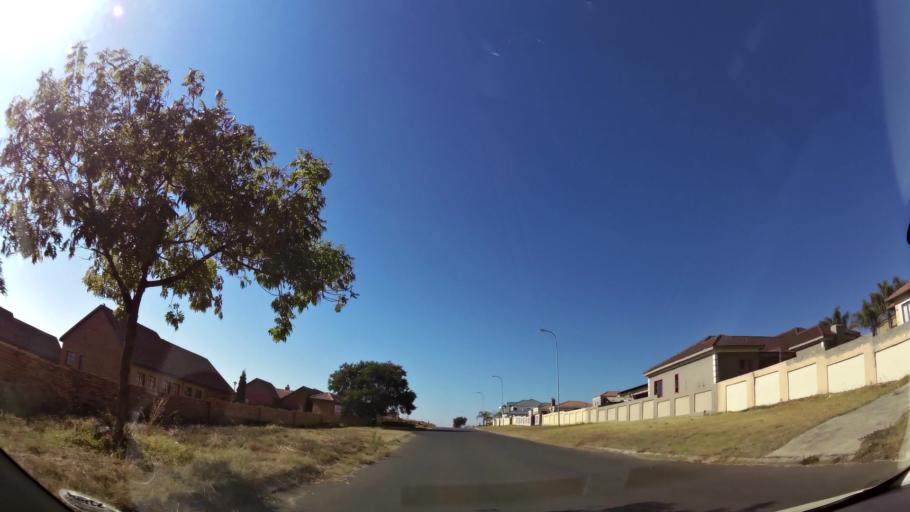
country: ZA
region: Mpumalanga
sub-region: Nkangala District Municipality
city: Witbank
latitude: -25.8644
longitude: 29.2506
